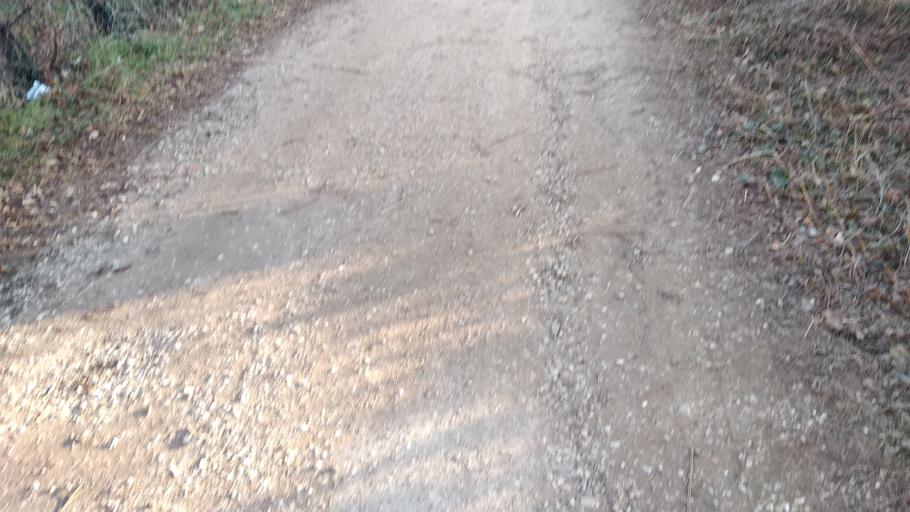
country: IT
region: Veneto
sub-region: Provincia di Vicenza
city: Schio
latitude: 45.6994
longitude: 11.3518
